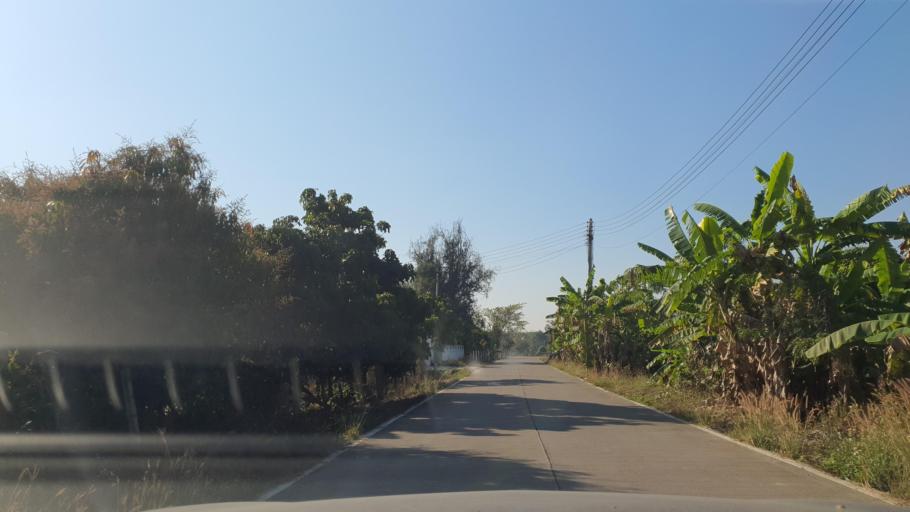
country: TH
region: Chiang Mai
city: Saraphi
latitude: 18.6860
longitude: 99.0803
